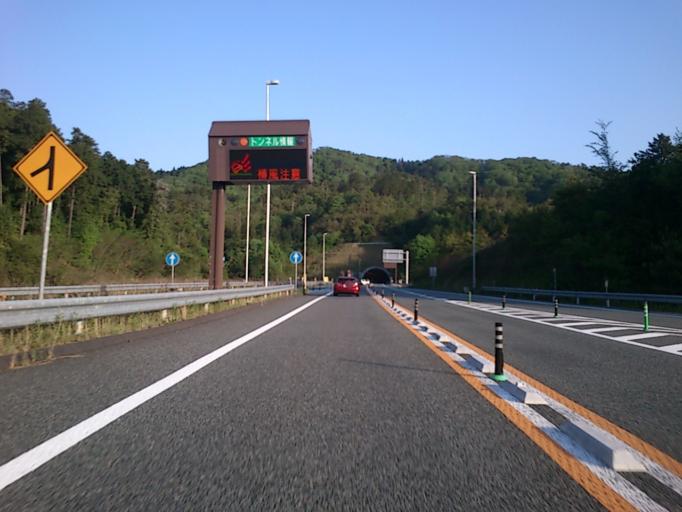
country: JP
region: Kyoto
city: Ayabe
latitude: 35.3340
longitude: 135.3102
